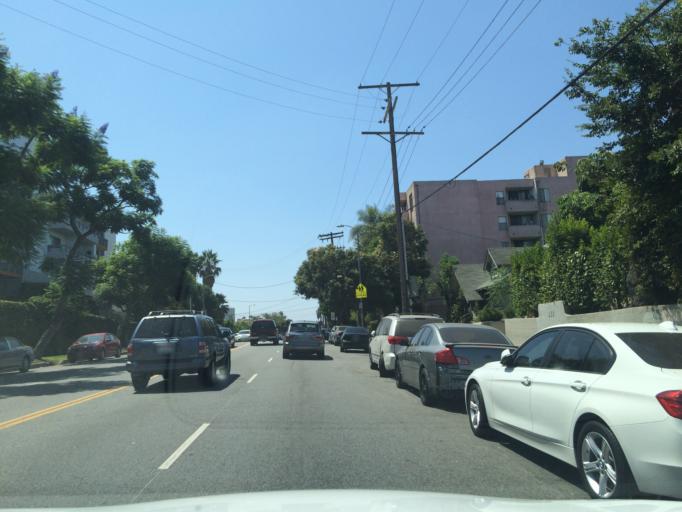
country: US
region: California
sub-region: Los Angeles County
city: Silver Lake
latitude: 34.0723
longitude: -118.2868
